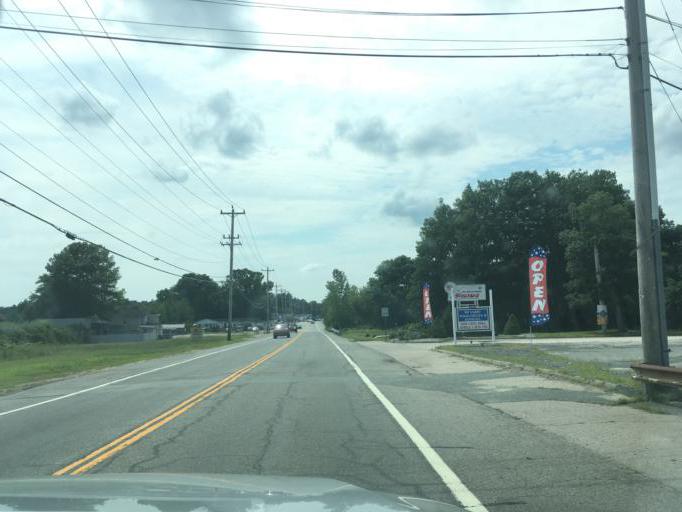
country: US
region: Rhode Island
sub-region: Kent County
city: West Warwick
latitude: 41.6853
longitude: -71.5504
